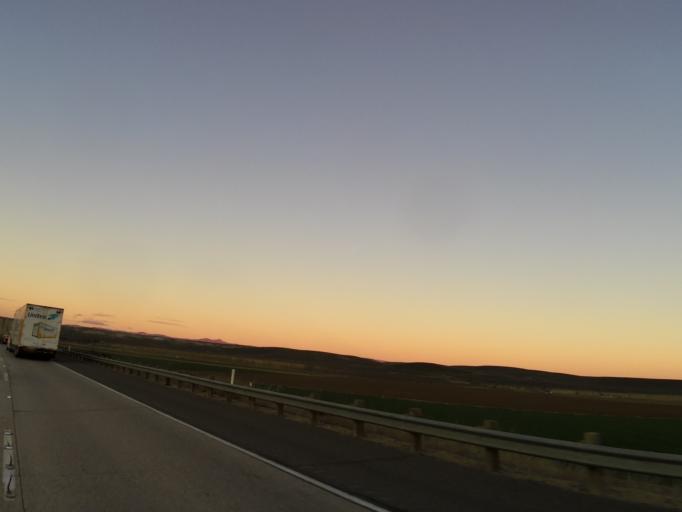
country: US
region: California
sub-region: Monterey County
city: King City
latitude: 36.1119
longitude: -121.0201
